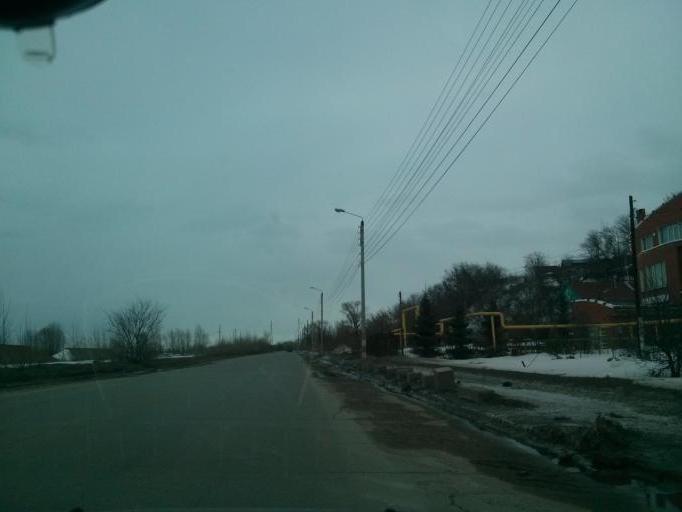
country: RU
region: Nizjnij Novgorod
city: Afonino
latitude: 56.3088
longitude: 44.0935
